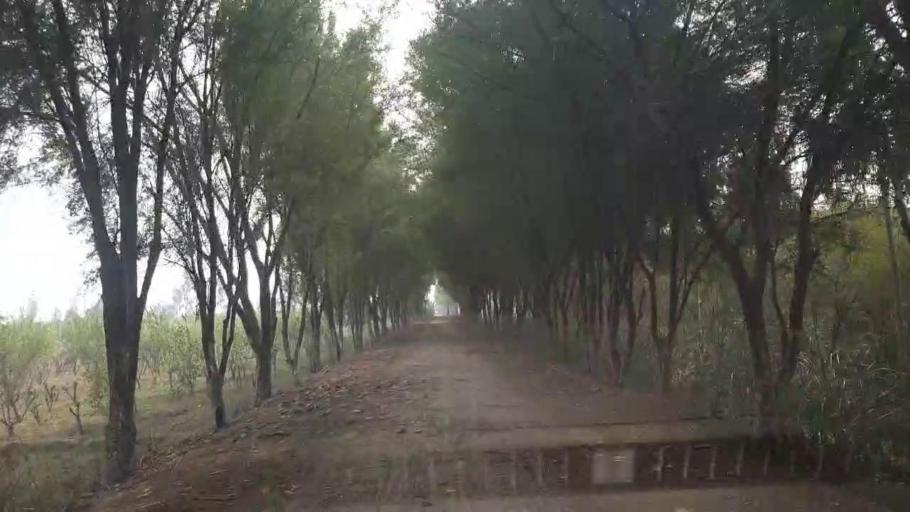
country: PK
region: Sindh
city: Tando Adam
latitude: 25.7765
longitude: 68.5852
